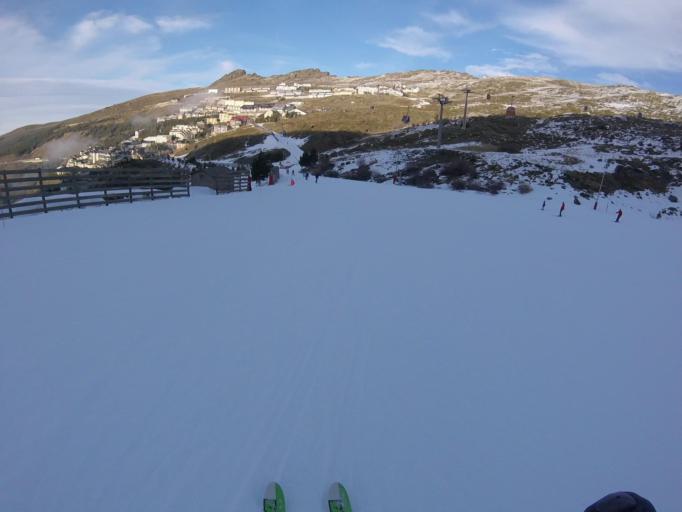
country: ES
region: Andalusia
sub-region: Provincia de Granada
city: Guejar-Sierra
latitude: 37.0883
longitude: -3.3984
